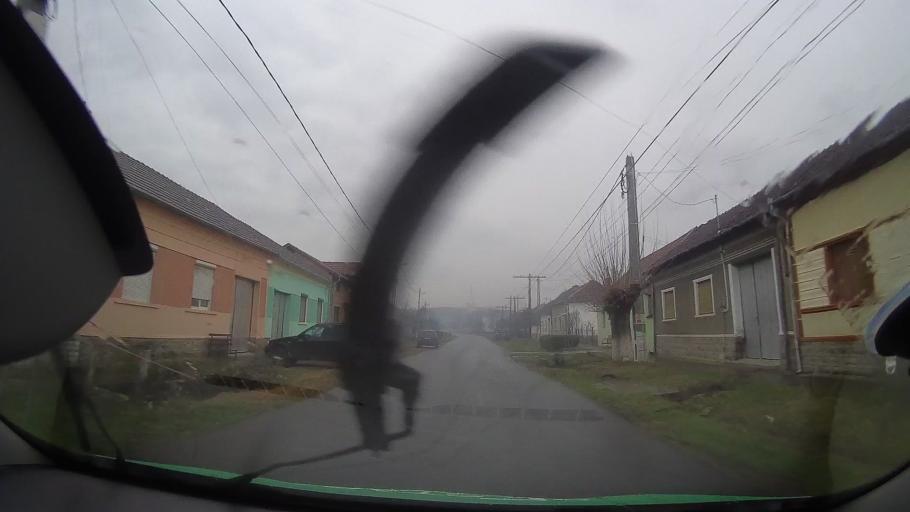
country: RO
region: Bihor
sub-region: Comuna Uileacu de Beius
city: Uileacu de Beius
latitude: 46.6832
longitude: 22.2230
